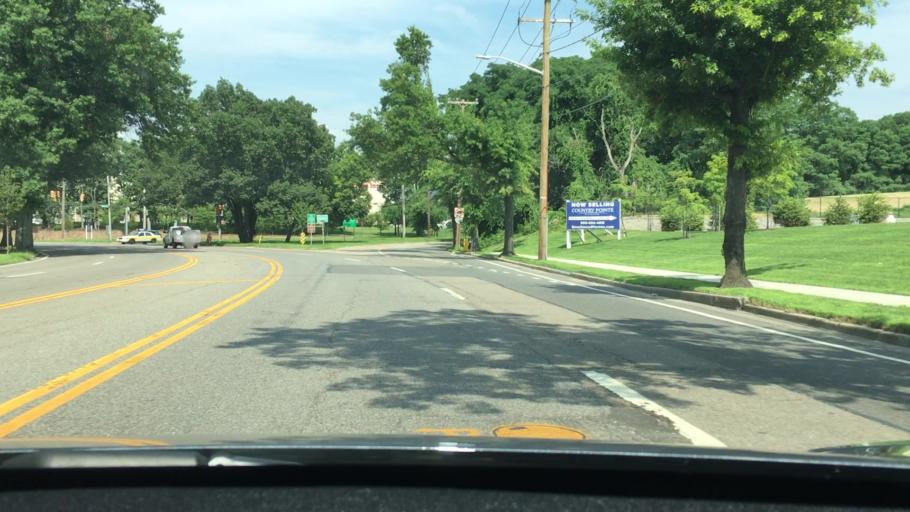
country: US
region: New York
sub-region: Nassau County
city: Old Bethpage
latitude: 40.7812
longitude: -73.4465
